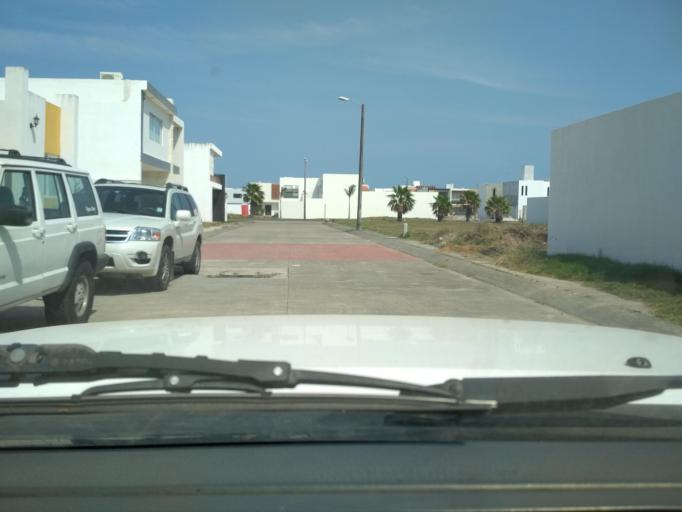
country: MX
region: Veracruz
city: Boca del Rio
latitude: 19.1041
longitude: -96.1258
